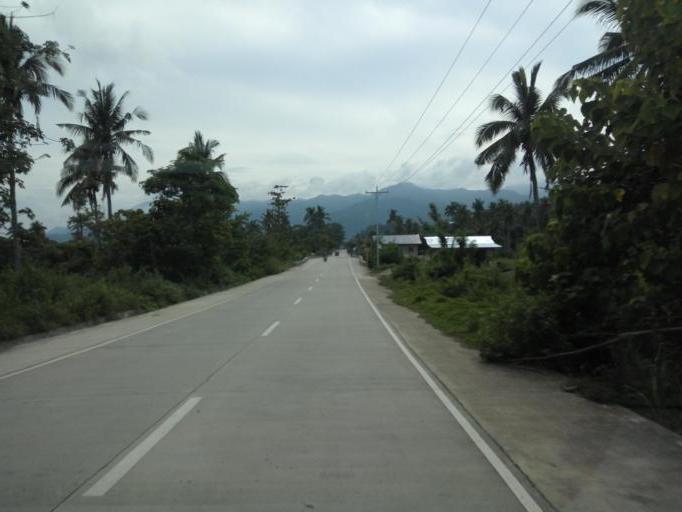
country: PH
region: Central Luzon
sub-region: Province of Aurora
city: Dinalongan
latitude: 16.0774
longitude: 121.7741
